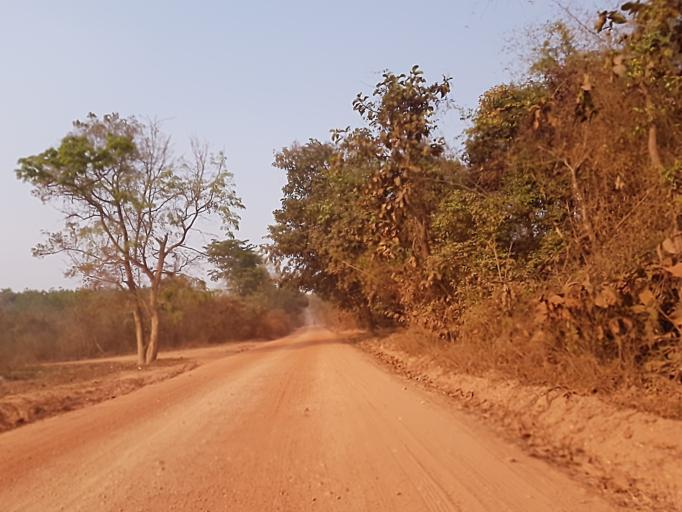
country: TH
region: Nong Khai
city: Phon Phisai
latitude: 18.0086
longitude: 102.9092
